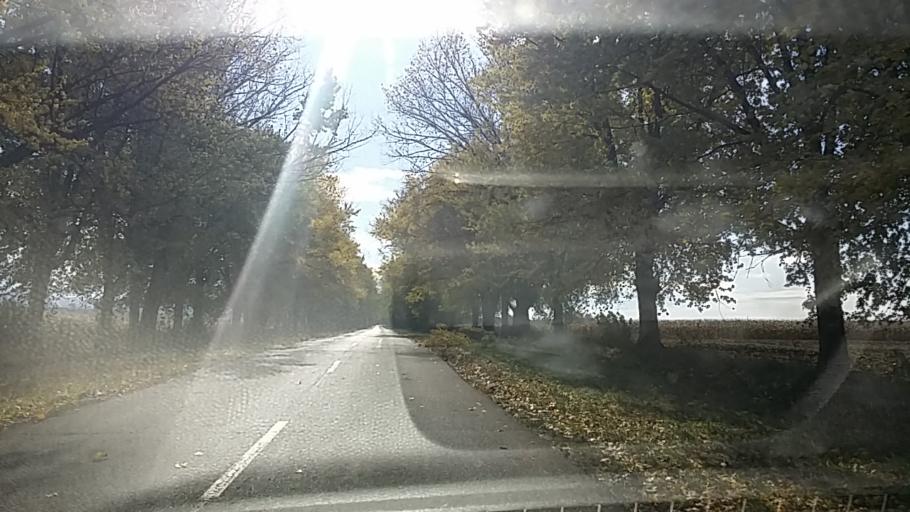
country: HU
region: Borsod-Abauj-Zemplen
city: Gonc
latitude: 48.4314
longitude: 21.2381
